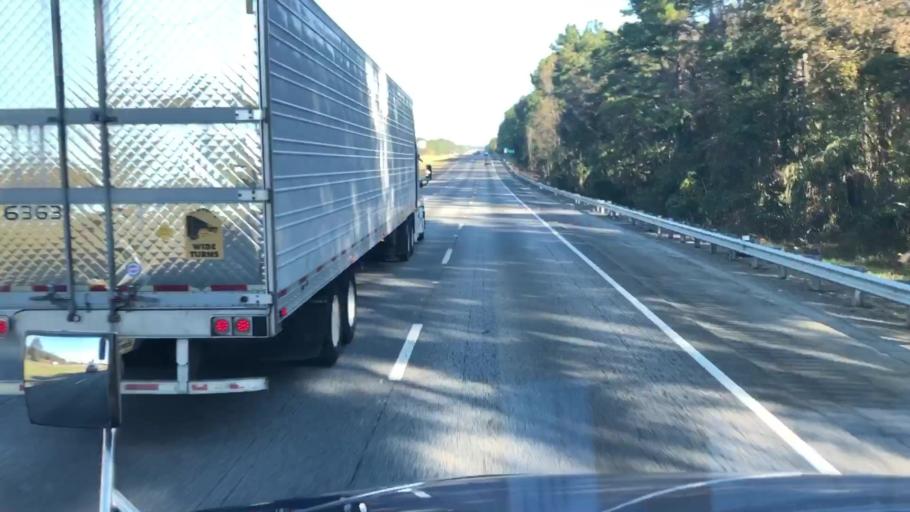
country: US
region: Georgia
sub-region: Dooly County
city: Unadilla
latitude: 32.3478
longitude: -83.7680
